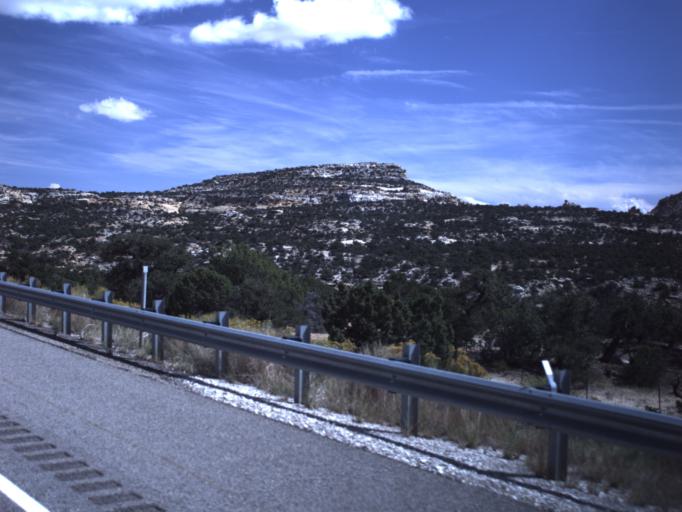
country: US
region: Utah
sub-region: Emery County
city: Ferron
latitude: 38.8592
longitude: -110.8247
